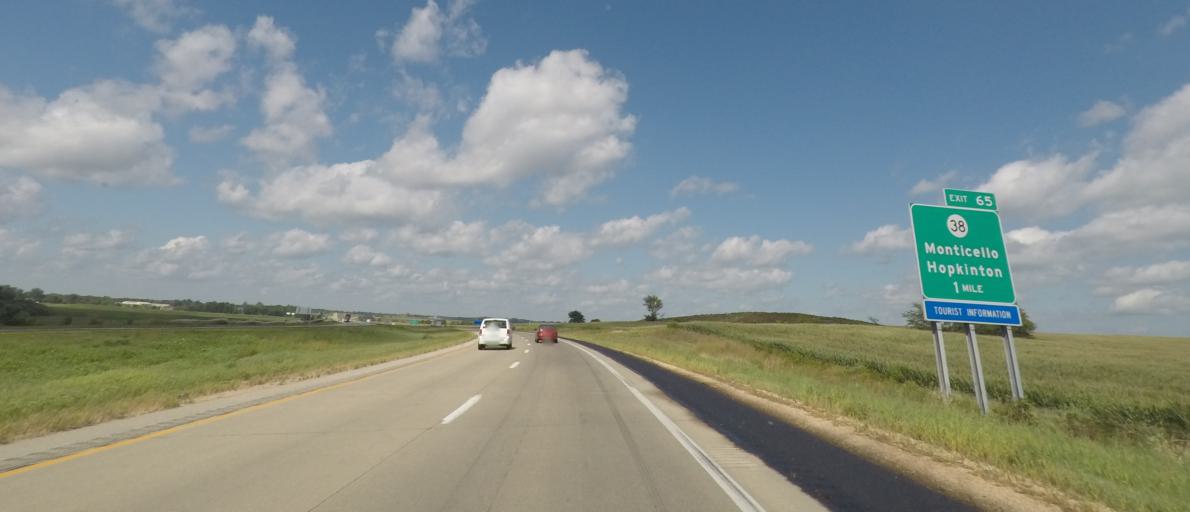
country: US
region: Iowa
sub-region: Jones County
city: Monticello
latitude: 42.2111
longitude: -91.1744
